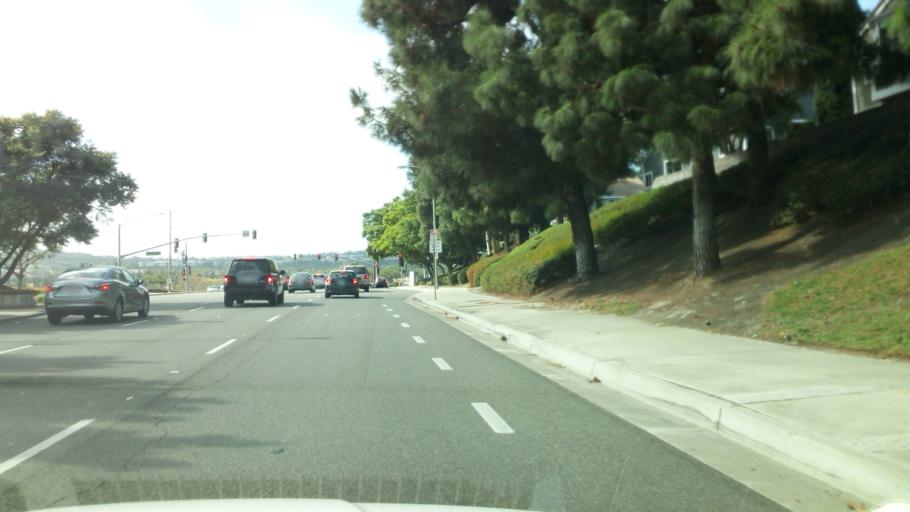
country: US
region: California
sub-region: Orange County
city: Aliso Viejo
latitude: 33.5708
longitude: -117.7130
